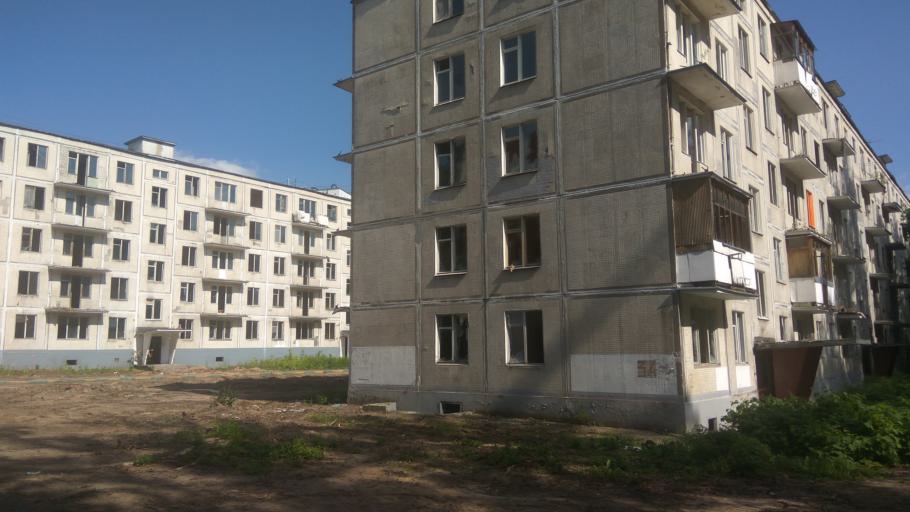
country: RU
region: Moskovskaya
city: Bol'shaya Setun'
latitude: 55.7459
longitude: 37.4062
